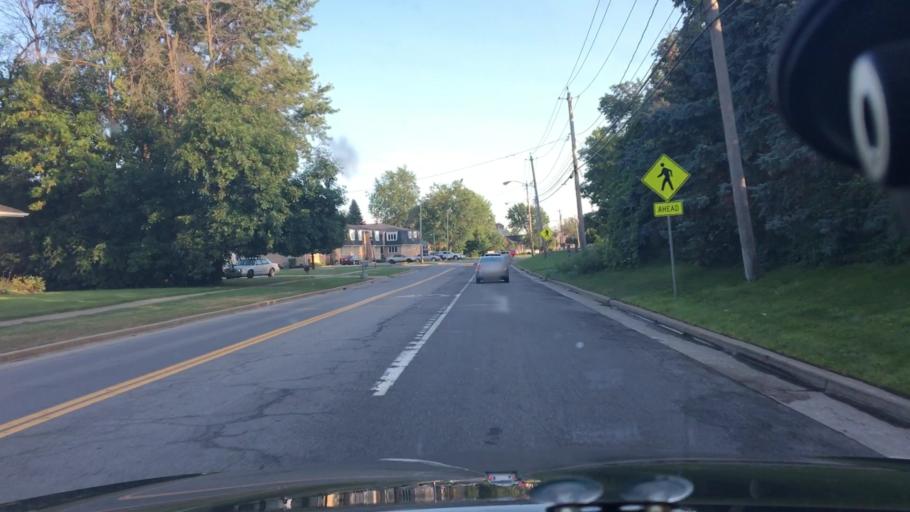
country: US
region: New York
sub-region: Erie County
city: Williamsville
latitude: 42.9960
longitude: -78.7601
